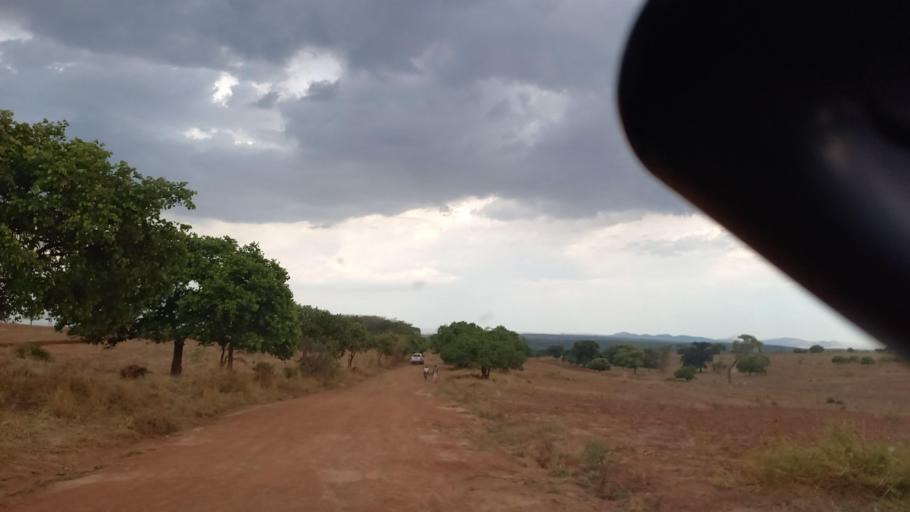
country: ZM
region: Lusaka
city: Kafue
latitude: -16.1342
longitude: 28.0563
